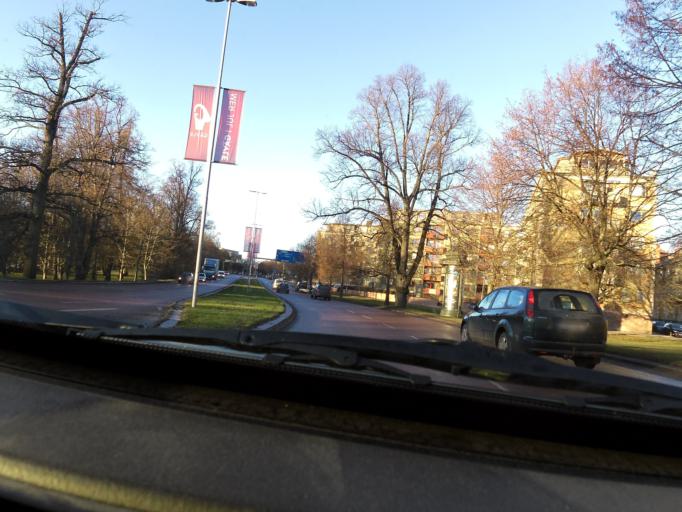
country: SE
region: Gaevleborg
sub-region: Gavle Kommun
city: Gavle
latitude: 60.6737
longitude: 17.1341
